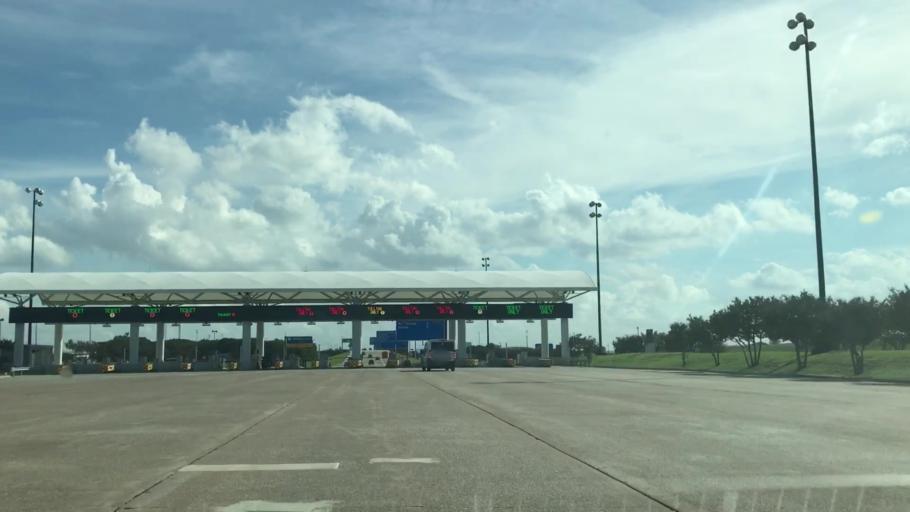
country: US
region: Texas
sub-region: Tarrant County
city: Grapevine
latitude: 32.9232
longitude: -97.0409
